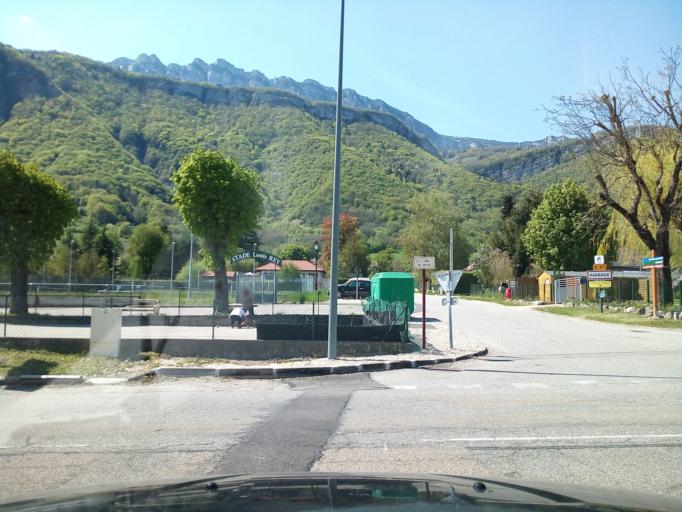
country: FR
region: Rhone-Alpes
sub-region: Departement de l'Isere
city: Barraux
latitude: 45.4337
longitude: 5.9824
